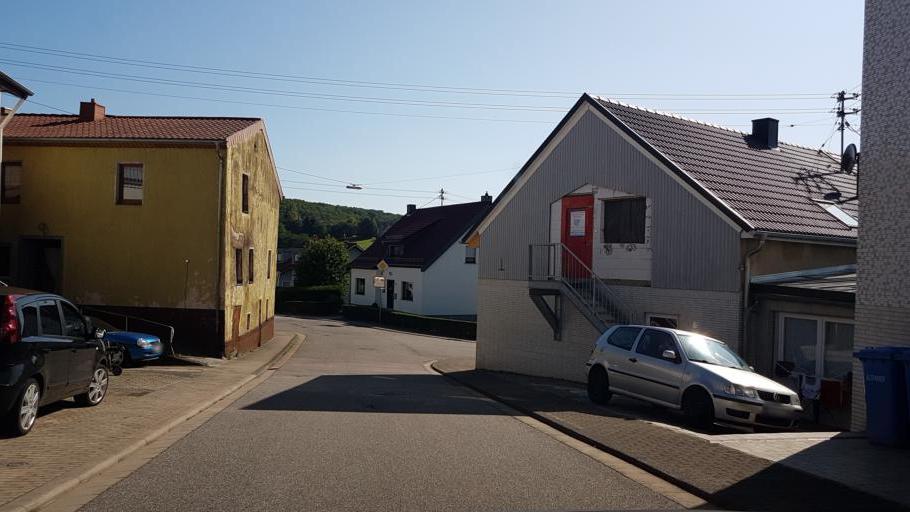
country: DE
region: Saarland
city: Lebach
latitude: 49.4766
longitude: 6.9031
